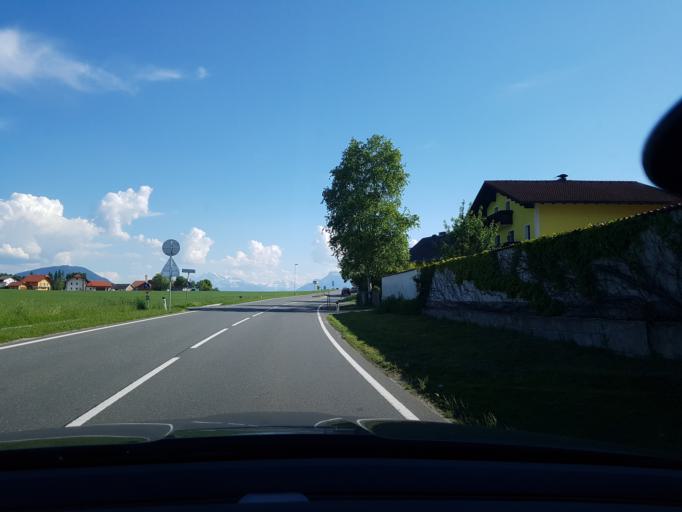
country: AT
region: Salzburg
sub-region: Politischer Bezirk Salzburg-Umgebung
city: Obertrum am See
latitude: 47.9081
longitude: 13.0812
